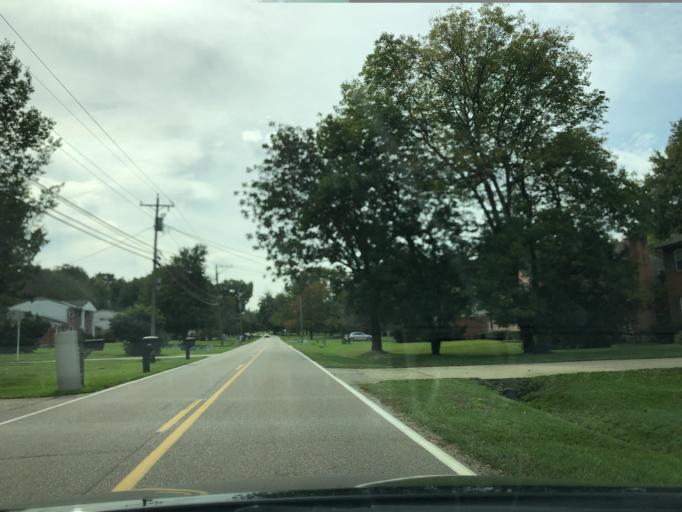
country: US
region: Ohio
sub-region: Hamilton County
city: The Village of Indian Hill
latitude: 39.2286
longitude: -84.3009
